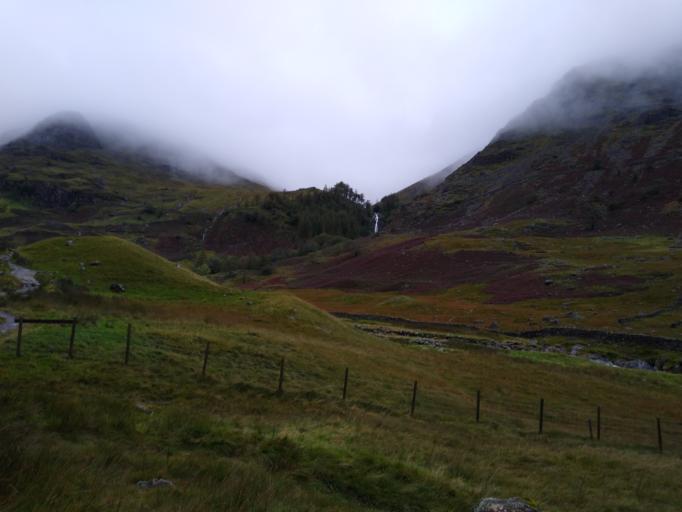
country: GB
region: England
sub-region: Cumbria
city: Keswick
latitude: 54.4917
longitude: -3.1827
